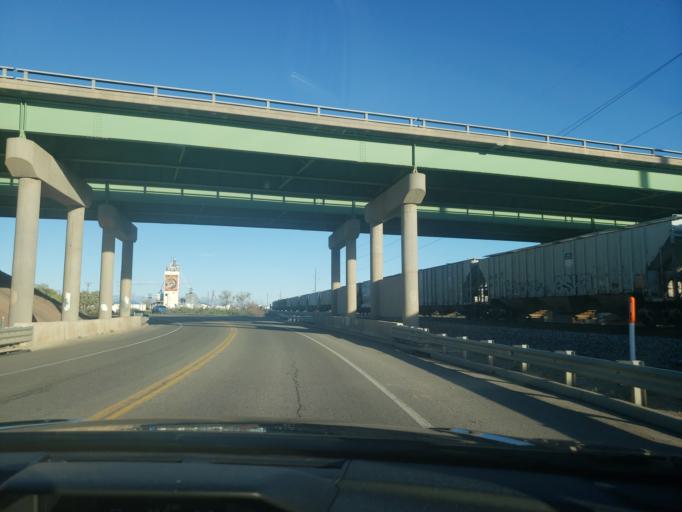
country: US
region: Colorado
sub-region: Mesa County
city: Fruita
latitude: 39.1569
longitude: -108.7369
